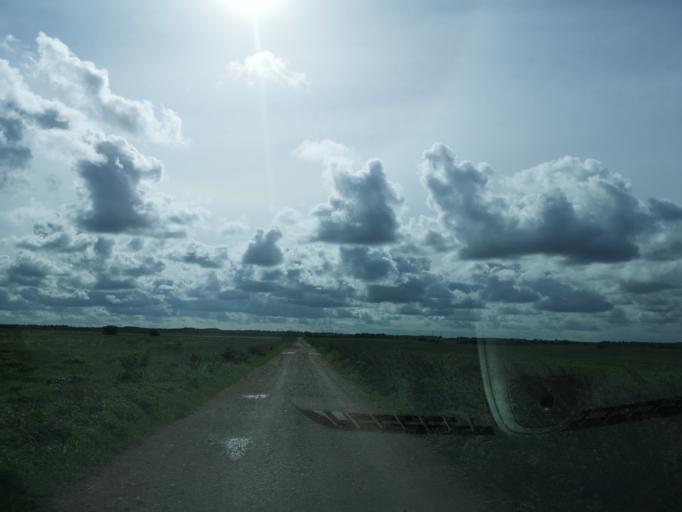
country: DK
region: Central Jutland
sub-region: Ringkobing-Skjern Kommune
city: Tarm
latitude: 55.9359
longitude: 8.5371
